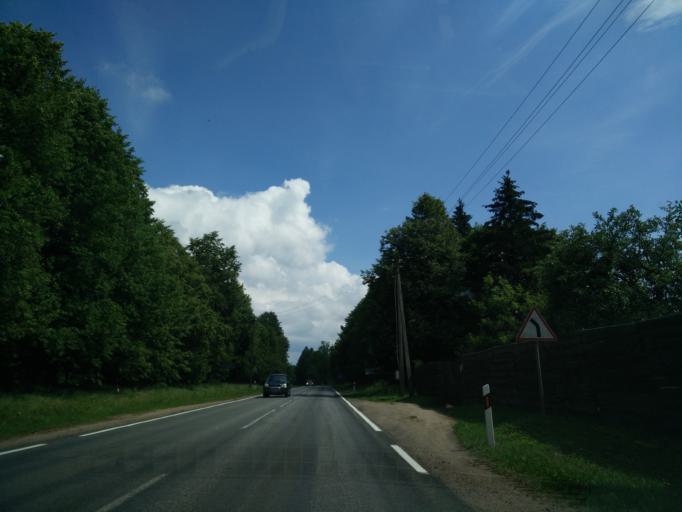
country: LT
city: Skaidiskes
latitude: 54.6920
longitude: 25.4626
